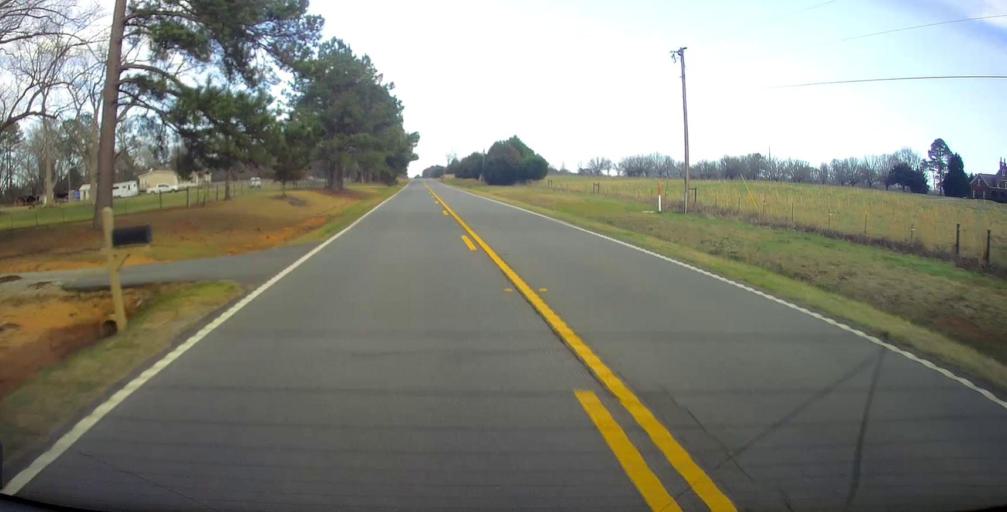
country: US
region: Georgia
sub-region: Harris County
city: Hamilton
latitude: 32.6843
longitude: -84.7600
